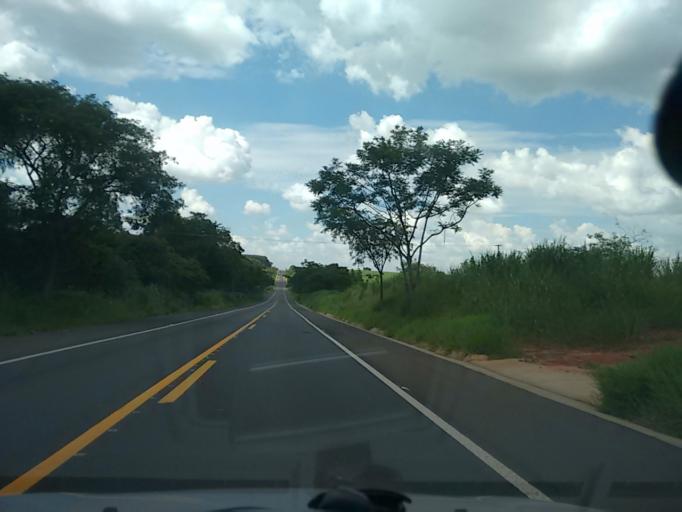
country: BR
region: Sao Paulo
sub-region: Osvaldo Cruz
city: Osvaldo Cruz
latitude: -21.8427
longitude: -50.8297
